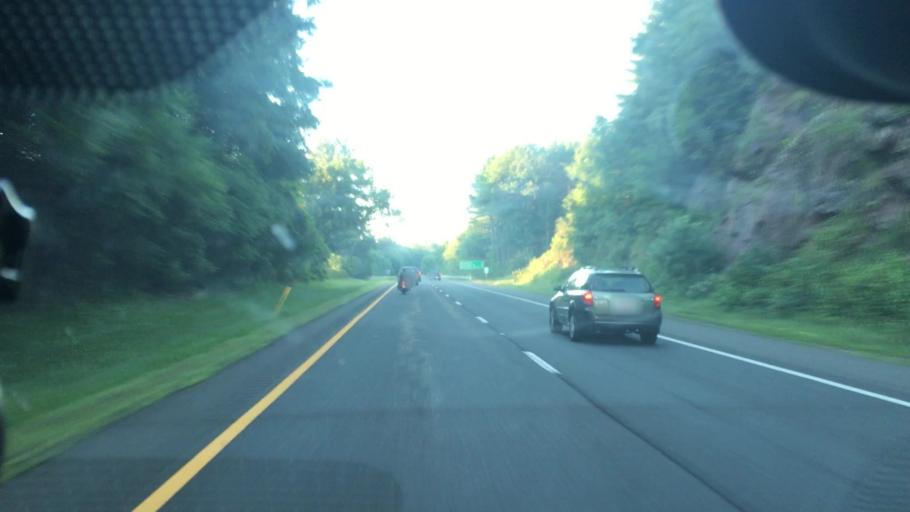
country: US
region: Massachusetts
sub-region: Franklin County
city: Turners Falls
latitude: 42.6282
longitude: -72.5830
